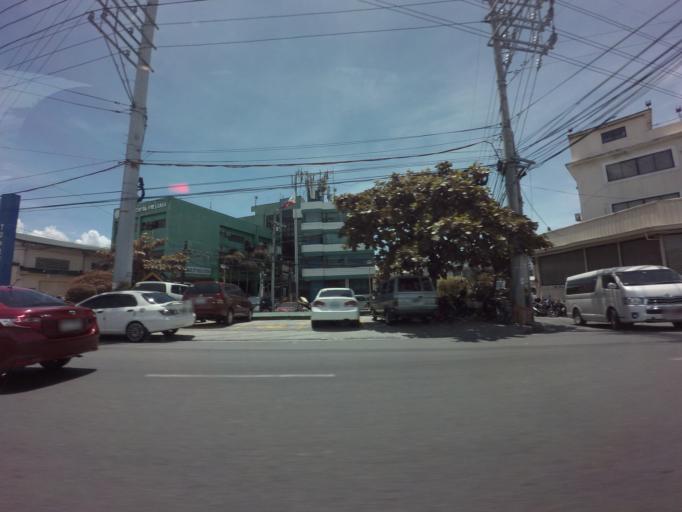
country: PH
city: Sambayanihan People's Village
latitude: 14.4864
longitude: 120.9913
